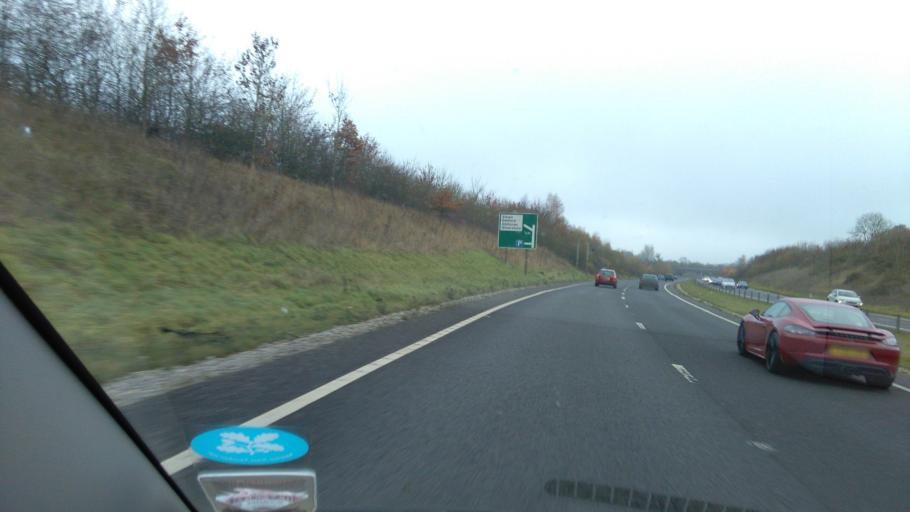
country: GB
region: England
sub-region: Northamptonshire
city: Silverstone
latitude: 52.0904
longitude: -1.0159
